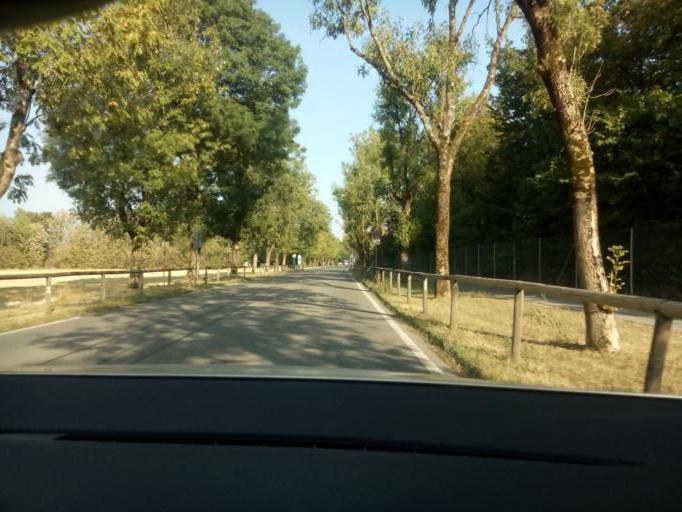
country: DE
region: Bavaria
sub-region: Upper Bavaria
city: Neubiberg
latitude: 48.0822
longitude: 11.6451
